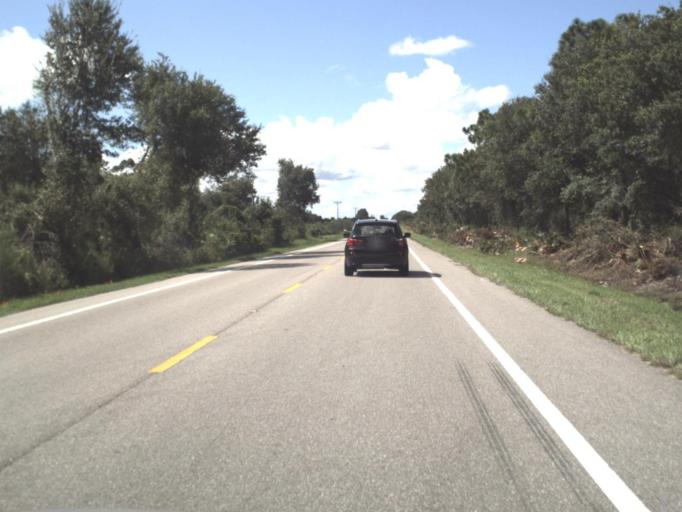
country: US
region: Florida
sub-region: Sarasota County
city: Lake Sarasota
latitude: 27.3676
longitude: -82.2111
